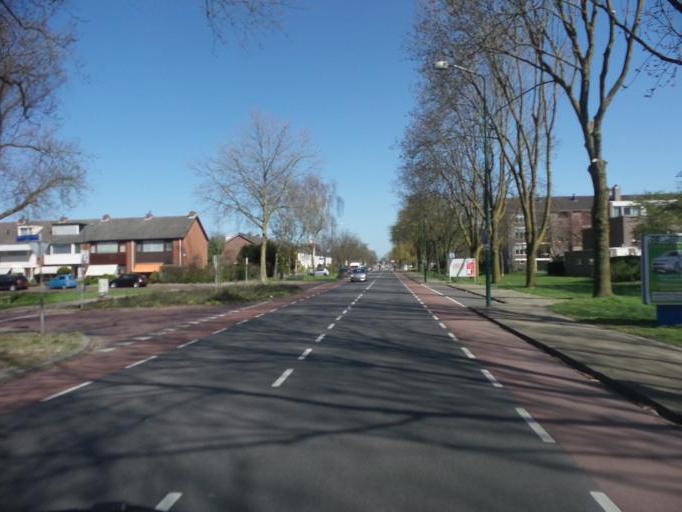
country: NL
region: Utrecht
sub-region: Gemeente Woerden
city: Woerden
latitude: 52.0867
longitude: 4.8648
